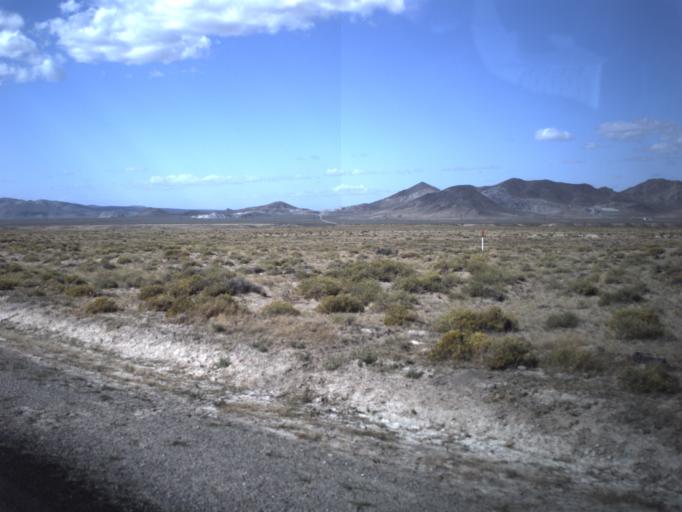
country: US
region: Utah
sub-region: Beaver County
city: Milford
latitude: 38.4685
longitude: -112.9973
